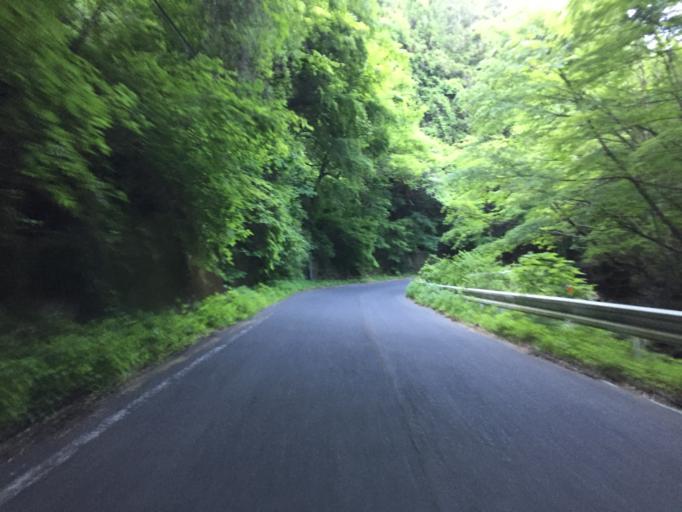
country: JP
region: Ibaraki
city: Kitaibaraki
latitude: 36.8786
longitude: 140.6322
